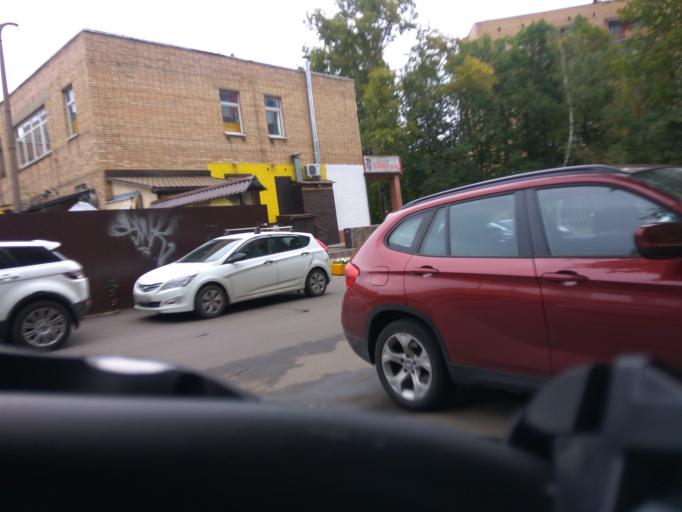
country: RU
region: Moscow
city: Tsaritsyno
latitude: 55.6454
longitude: 37.6596
